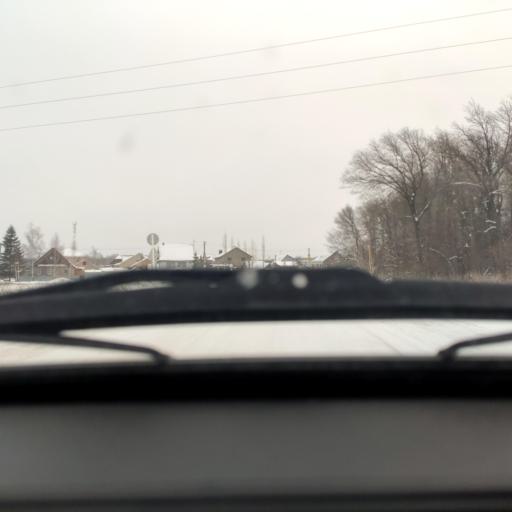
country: RU
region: Bashkortostan
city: Mikhaylovka
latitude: 54.8540
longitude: 55.8755
